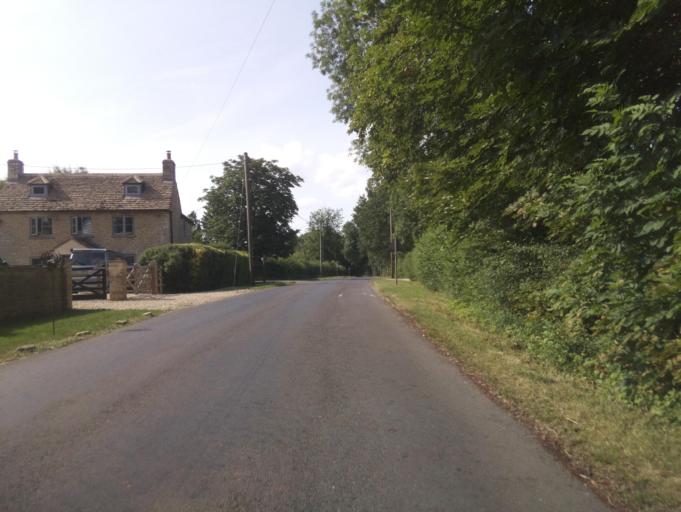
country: GB
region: England
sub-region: Wiltshire
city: Minety
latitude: 51.6205
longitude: -1.9666
